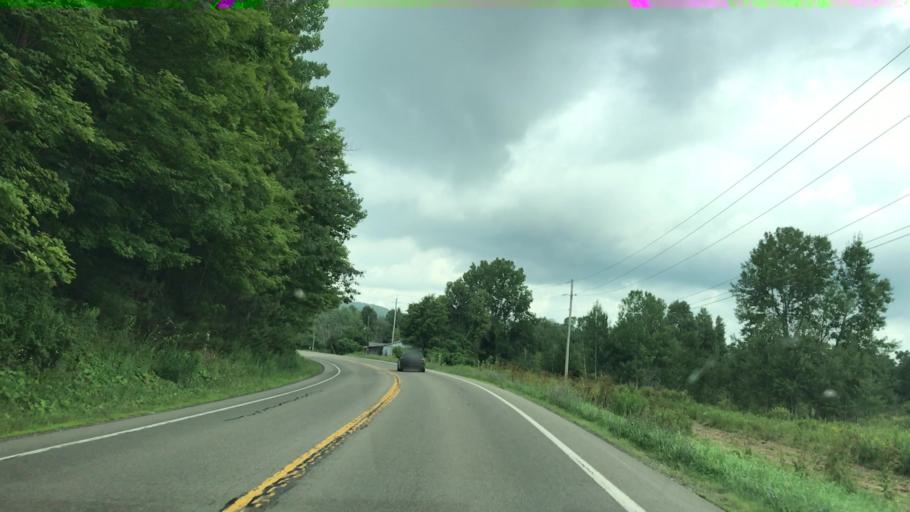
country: US
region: New York
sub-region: Steuben County
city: Bath
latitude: 42.4007
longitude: -77.3491
